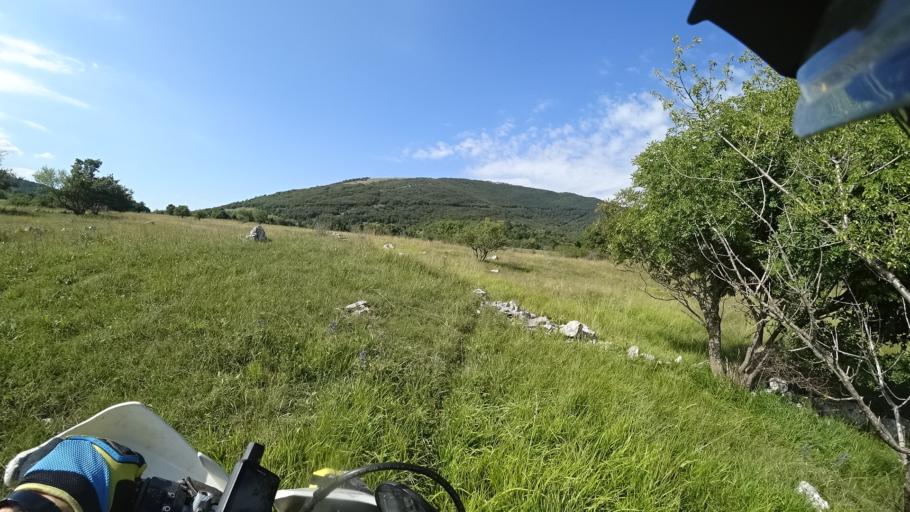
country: HR
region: Zadarska
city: Gracac
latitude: 44.3340
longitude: 15.9624
